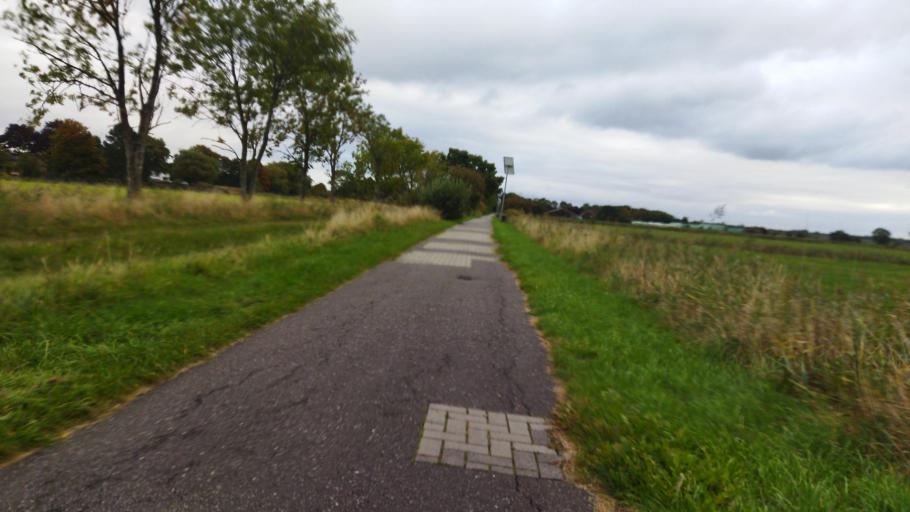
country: DE
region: Lower Saxony
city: Hinte
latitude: 53.4019
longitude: 7.1971
